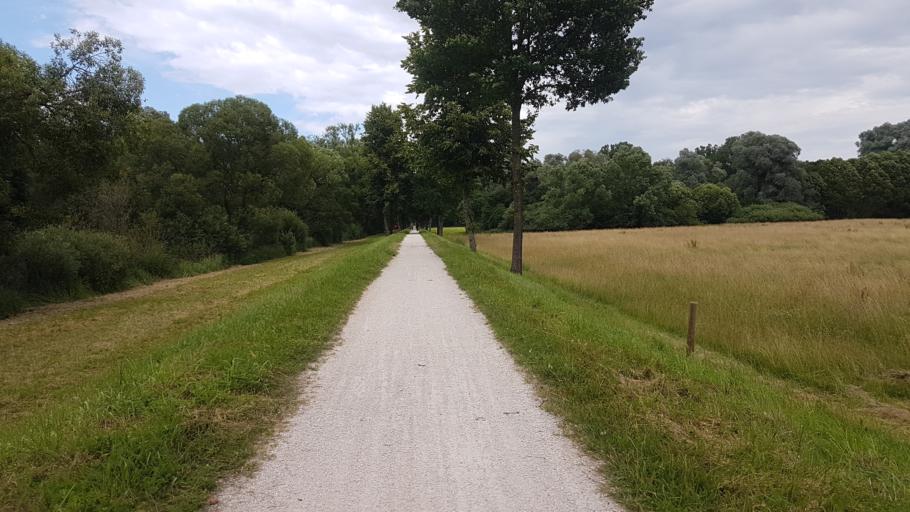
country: DE
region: Baden-Wuerttemberg
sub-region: Tuebingen Region
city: Neufra
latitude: 48.1326
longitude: 9.4625
